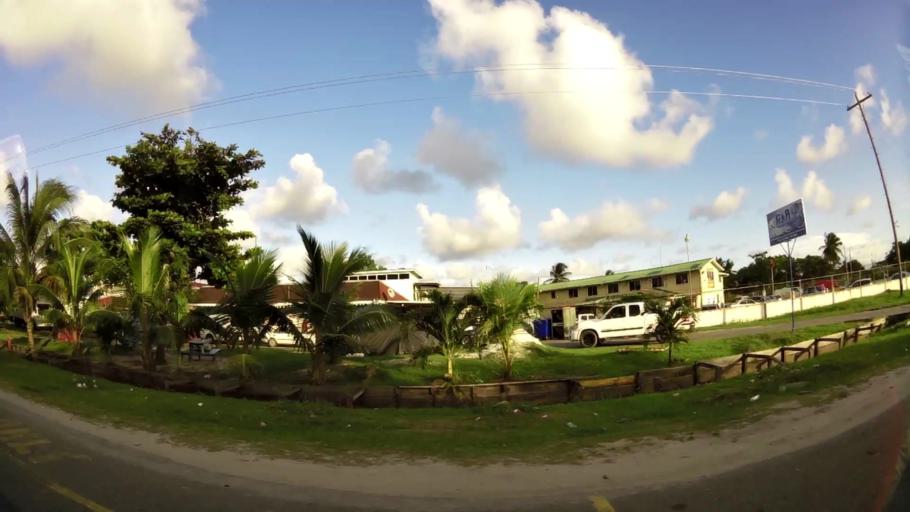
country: GY
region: Demerara-Mahaica
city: Georgetown
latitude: 6.7926
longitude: -58.1439
